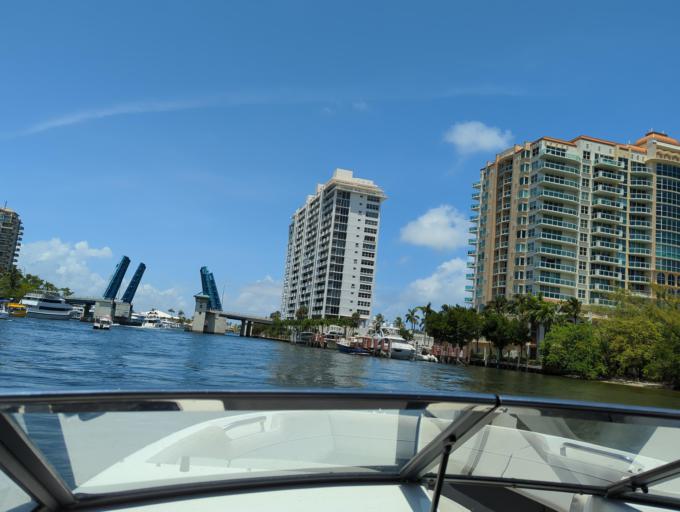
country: US
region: Florida
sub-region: Broward County
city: Sunrise
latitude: 26.1357
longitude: -80.1083
